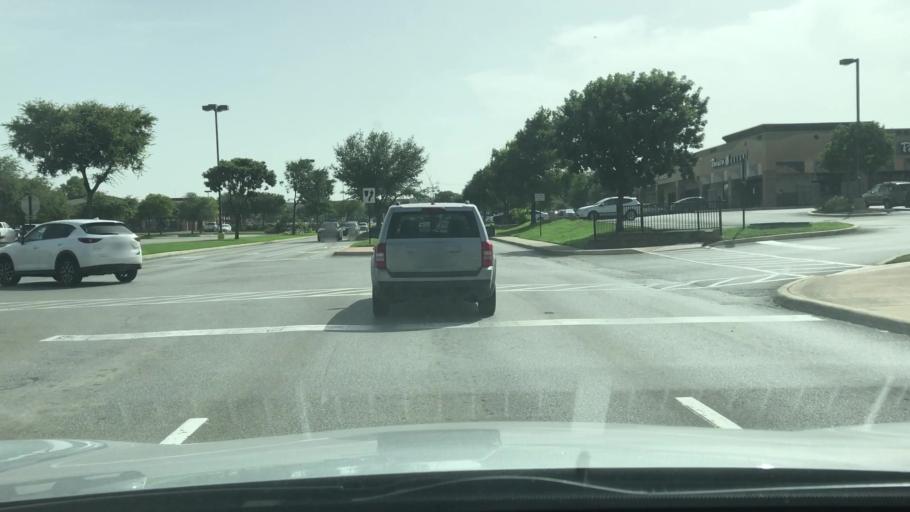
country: US
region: Texas
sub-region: Bexar County
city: Live Oak
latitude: 29.5705
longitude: -98.3274
